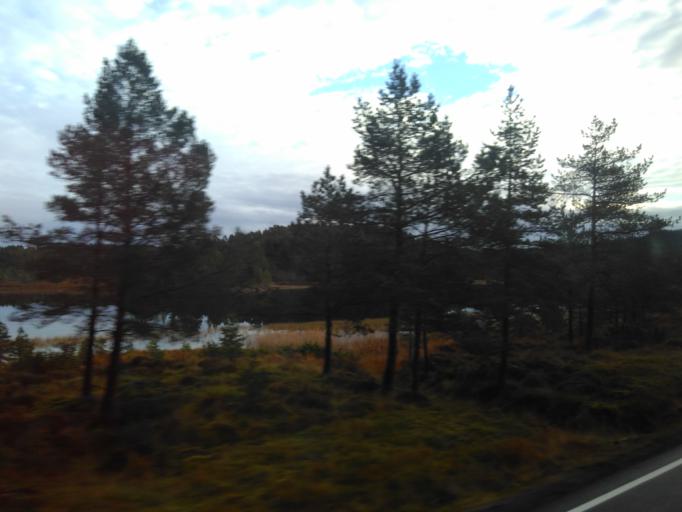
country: NO
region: Sor-Trondelag
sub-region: Hitra
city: Fillan
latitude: 63.5620
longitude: 9.0443
